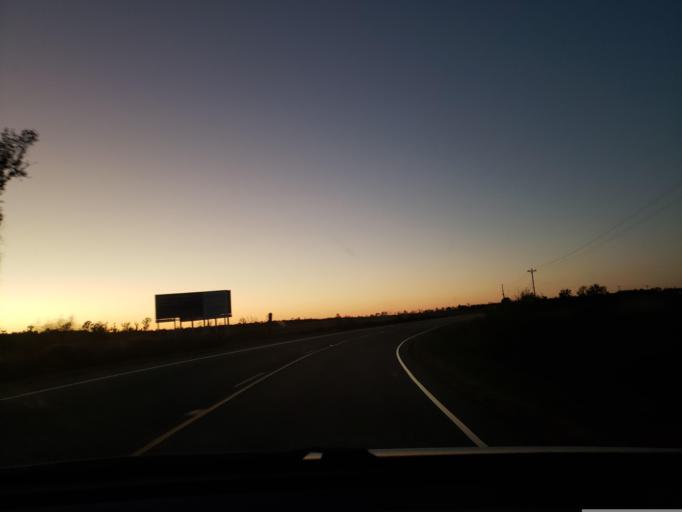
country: US
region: North Carolina
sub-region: Duplin County
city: Kenansville
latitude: 34.8884
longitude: -77.9043
